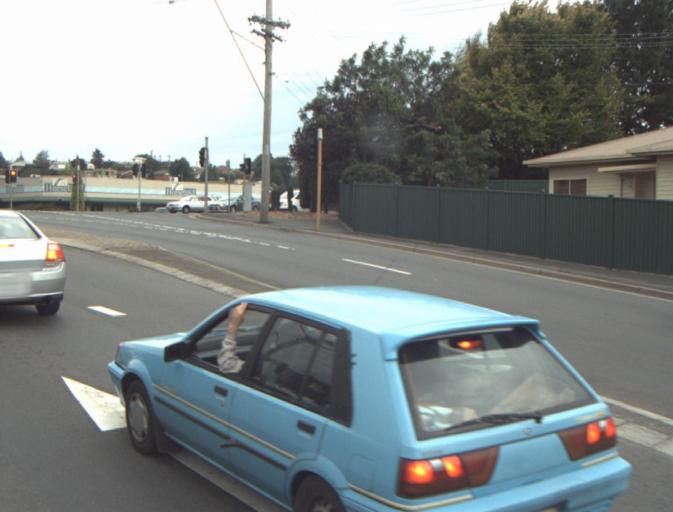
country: AU
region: Tasmania
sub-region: Launceston
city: East Launceston
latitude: -41.4603
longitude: 147.1556
